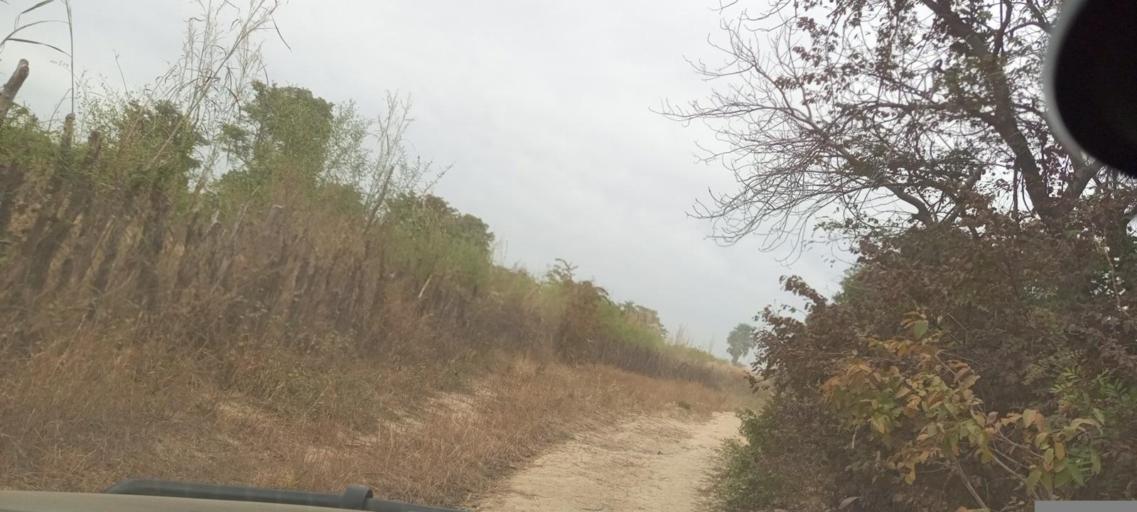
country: ML
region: Koulikoro
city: Kati
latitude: 12.7447
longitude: -8.3329
